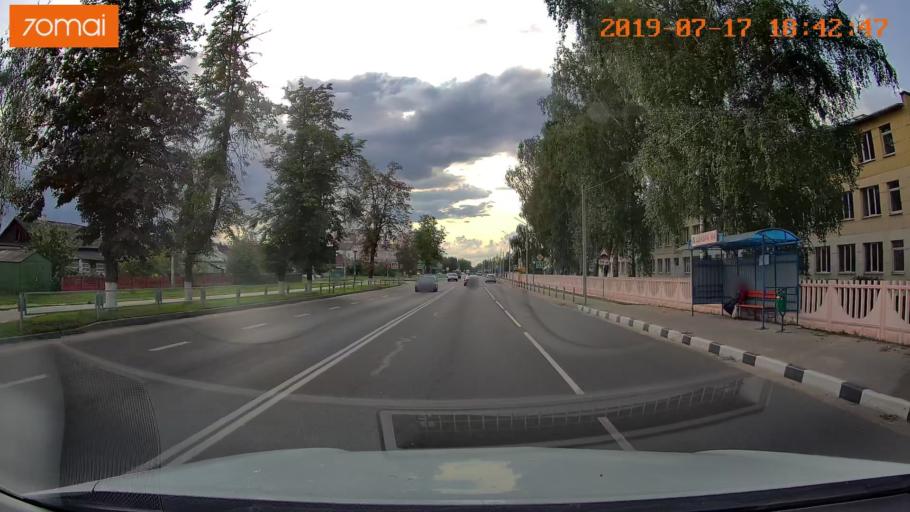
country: BY
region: Mogilev
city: Asipovichy
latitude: 53.3113
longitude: 28.6452
